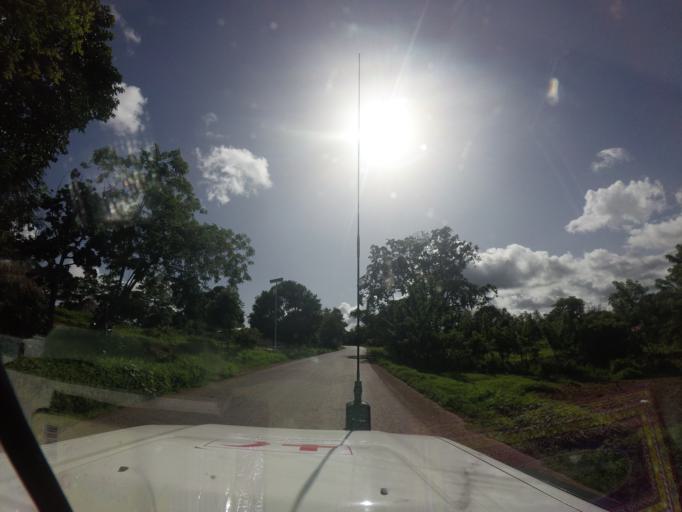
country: GN
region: Mamou
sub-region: Mamou Prefecture
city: Mamou
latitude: 10.3117
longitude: -12.2371
